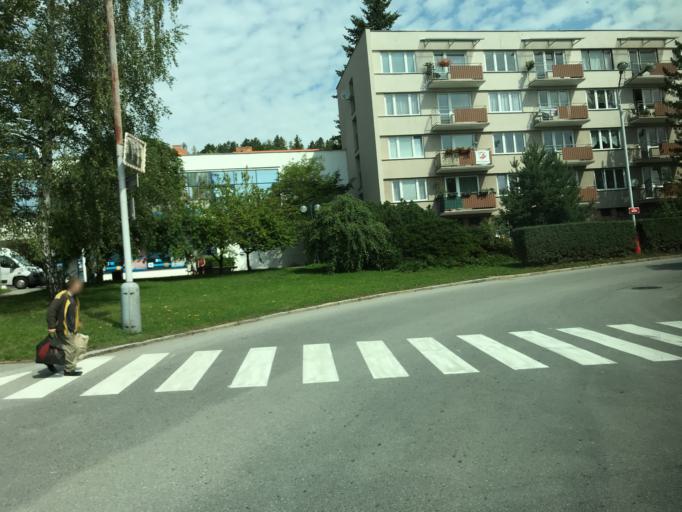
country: CZ
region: Jihocesky
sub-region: Okres Cesky Krumlov
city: Cesky Krumlov
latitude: 48.8156
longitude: 14.3153
